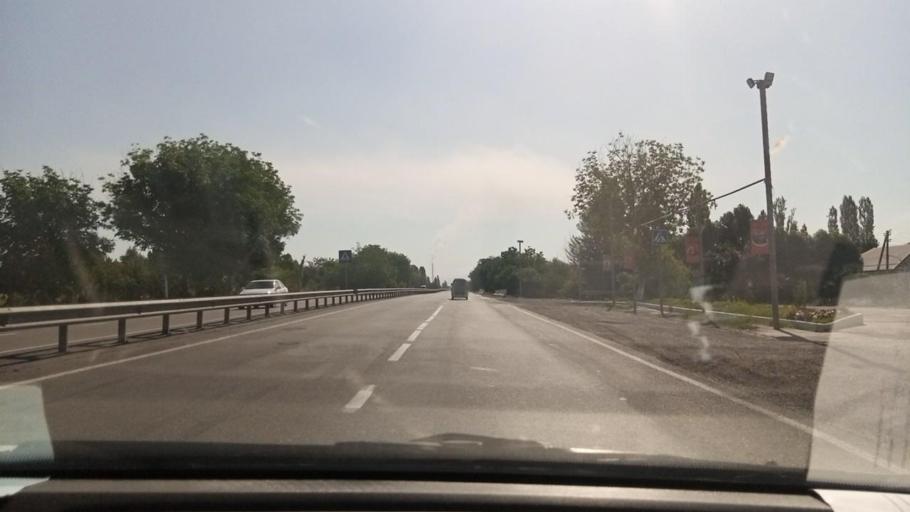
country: UZ
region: Toshkent
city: Ohangaron
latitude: 40.9018
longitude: 69.7109
